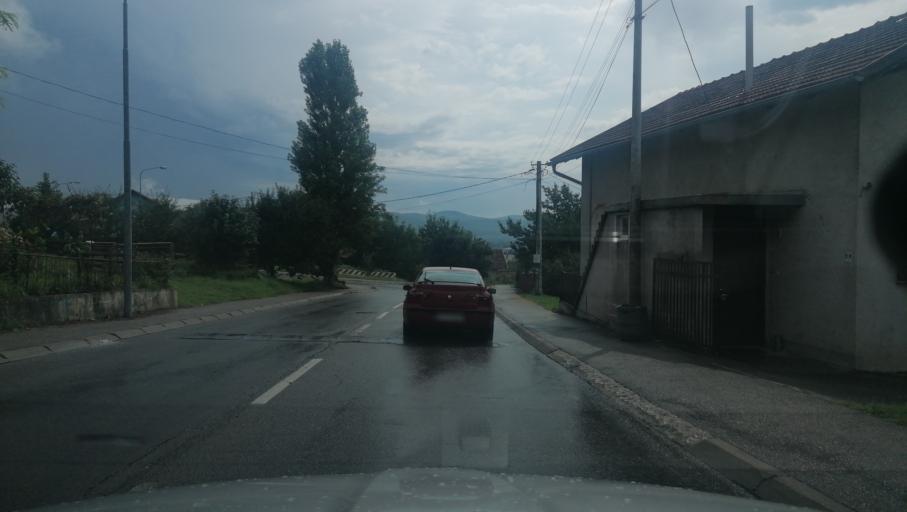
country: BA
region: Republika Srpska
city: Banja Luka
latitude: 44.7900
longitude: 17.1846
